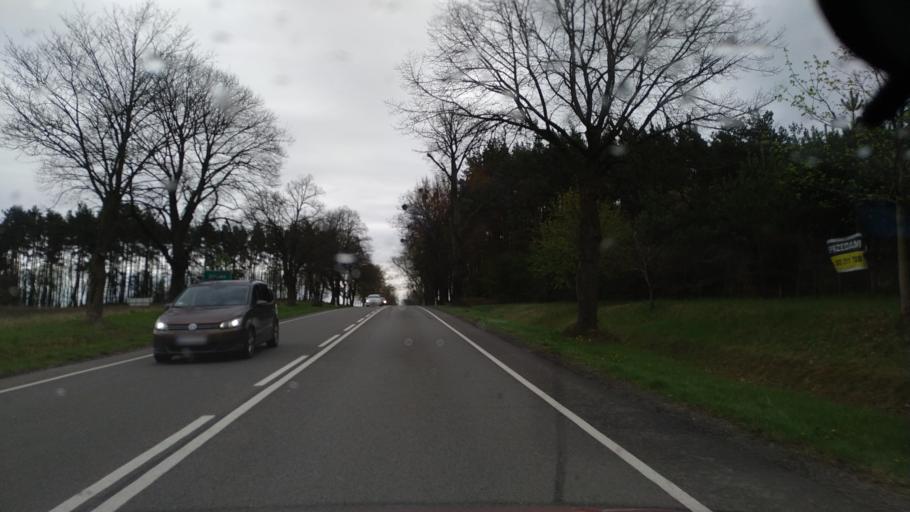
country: PL
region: Pomeranian Voivodeship
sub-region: Powiat starogardzki
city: Zblewo
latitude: 53.9321
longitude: 18.3551
